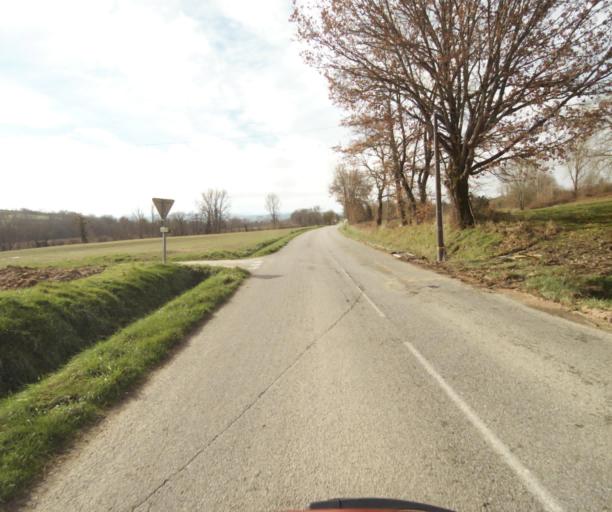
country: FR
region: Midi-Pyrenees
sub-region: Departement de l'Ariege
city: Pamiers
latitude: 43.1337
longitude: 1.5575
